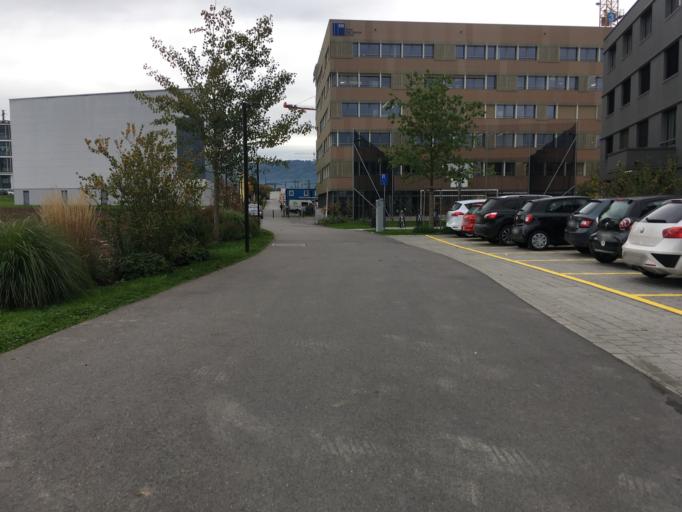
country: CH
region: Lucerne
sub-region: Lucerne-Land District
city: Meierskappel
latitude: 47.1458
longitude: 8.4362
